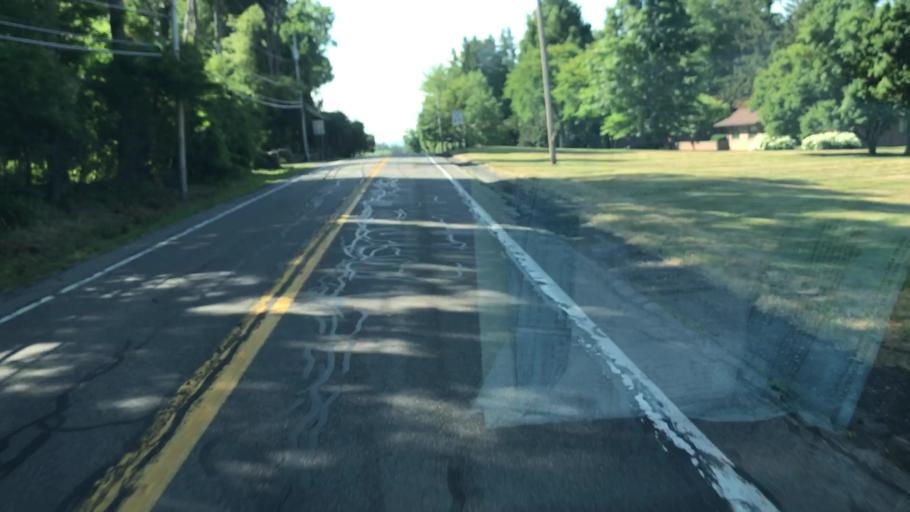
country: US
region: New York
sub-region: Onondaga County
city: Skaneateles
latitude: 42.9343
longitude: -76.4095
